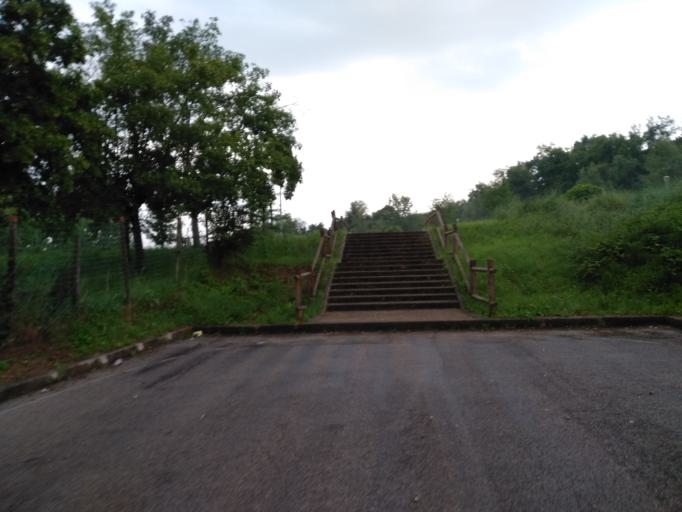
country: IT
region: Tuscany
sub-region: Province of Arezzo
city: San Giovanni Valdarno
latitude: 43.5588
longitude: 11.5261
